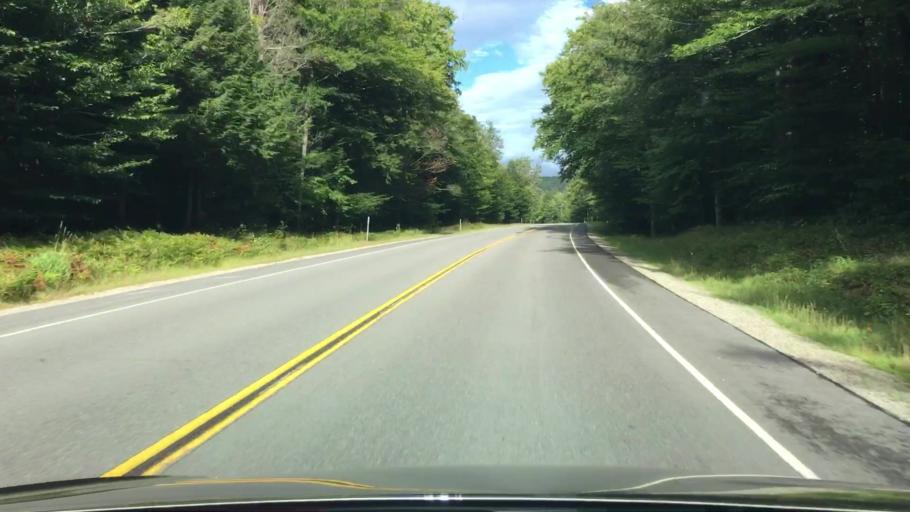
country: US
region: New Hampshire
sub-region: Carroll County
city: Tamworth
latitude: 43.9908
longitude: -71.2963
